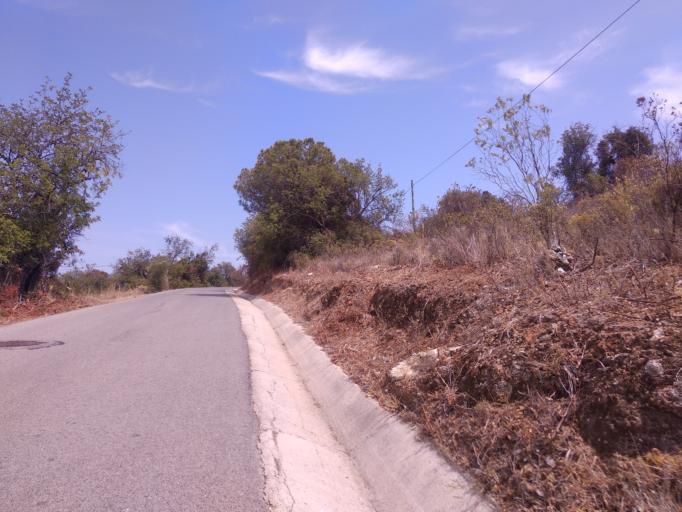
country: PT
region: Faro
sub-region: Loule
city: Almancil
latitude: 37.0783
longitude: -7.9993
